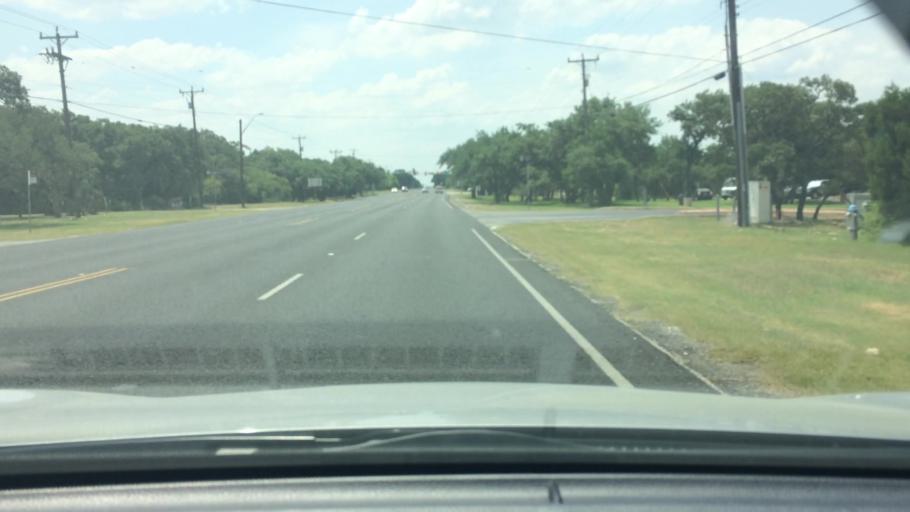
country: US
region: Texas
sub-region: Bexar County
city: Shavano Park
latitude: 29.5866
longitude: -98.5549
